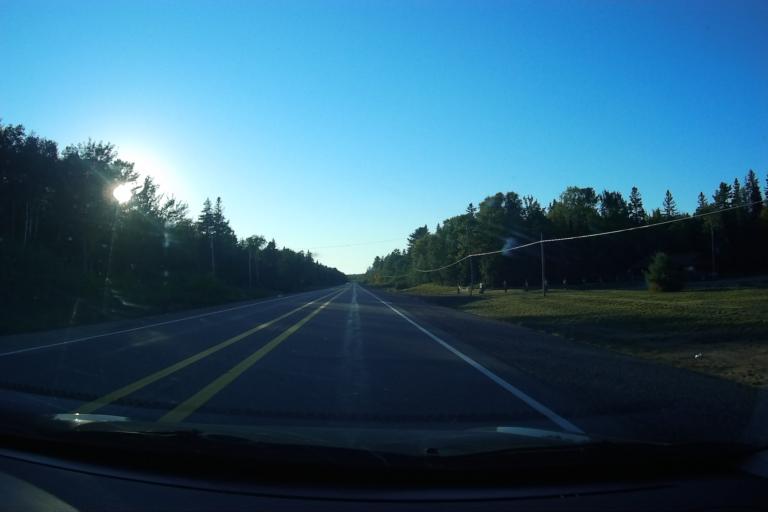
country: CA
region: Ontario
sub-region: Algoma
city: Sault Ste. Marie
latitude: 46.9648
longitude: -84.6670
